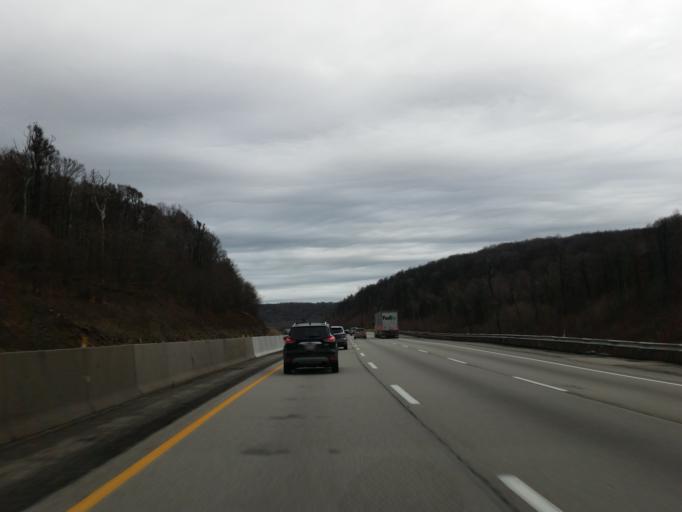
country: US
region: Pennsylvania
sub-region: Westmoreland County
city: Ligonier
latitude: 40.1115
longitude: -79.2477
